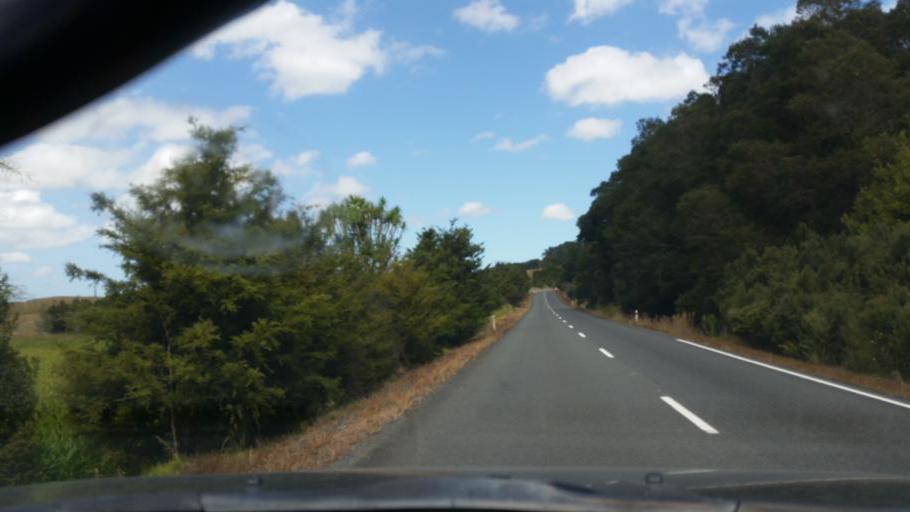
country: NZ
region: Northland
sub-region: Kaipara District
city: Dargaville
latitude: -35.8675
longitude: 173.8434
